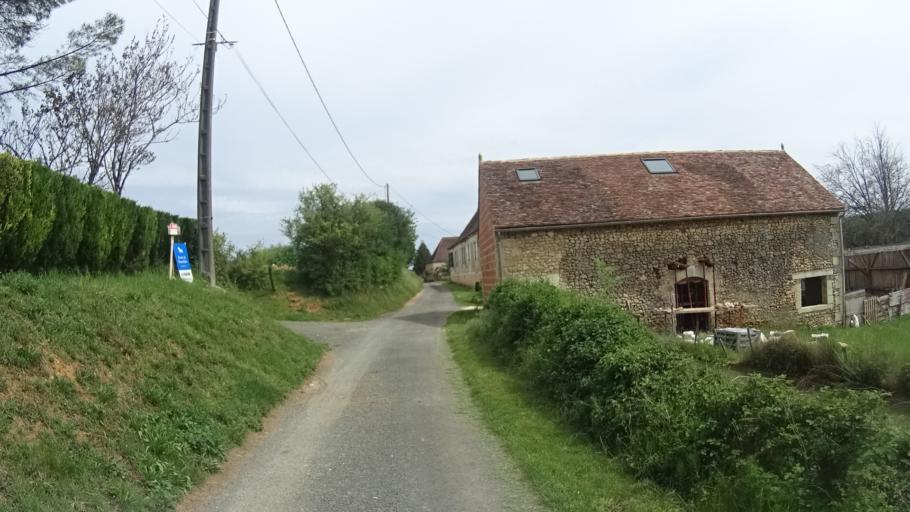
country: FR
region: Aquitaine
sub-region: Departement de la Dordogne
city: Lembras
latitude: 44.9958
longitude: 0.5330
